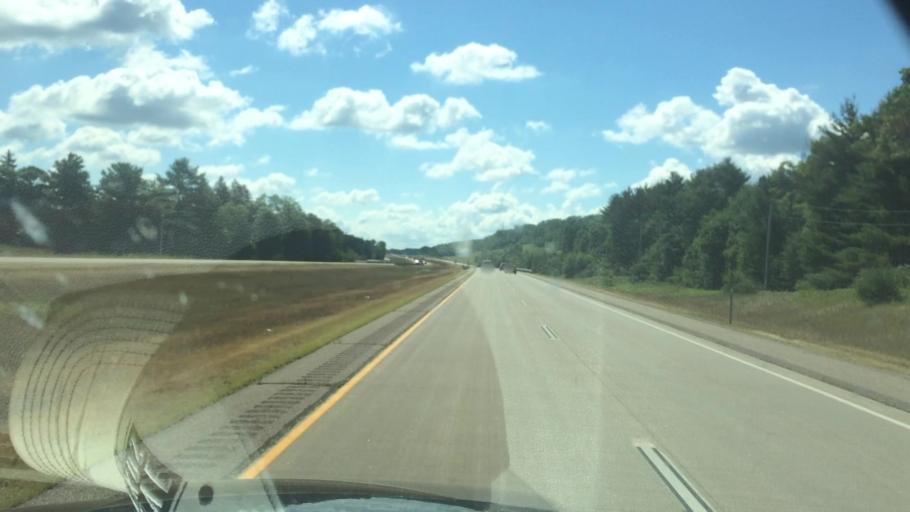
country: US
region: Wisconsin
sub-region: Waupaca County
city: King
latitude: 44.3790
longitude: -89.1710
